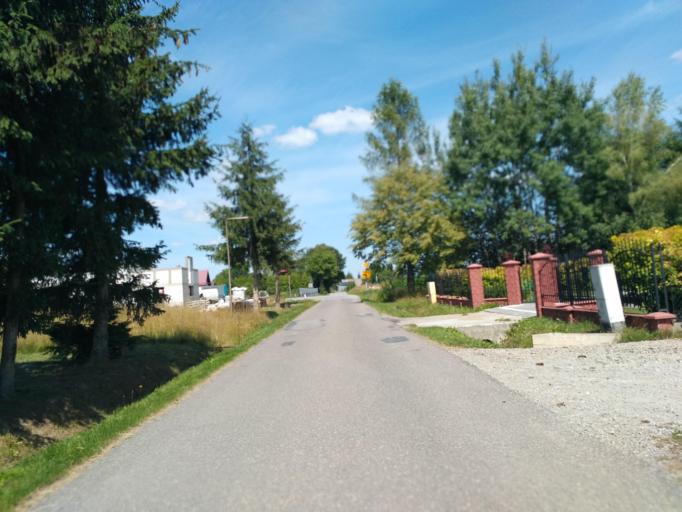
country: PL
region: Subcarpathian Voivodeship
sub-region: Powiat krosnienski
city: Kroscienko Wyzne
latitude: 49.6526
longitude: 21.8466
